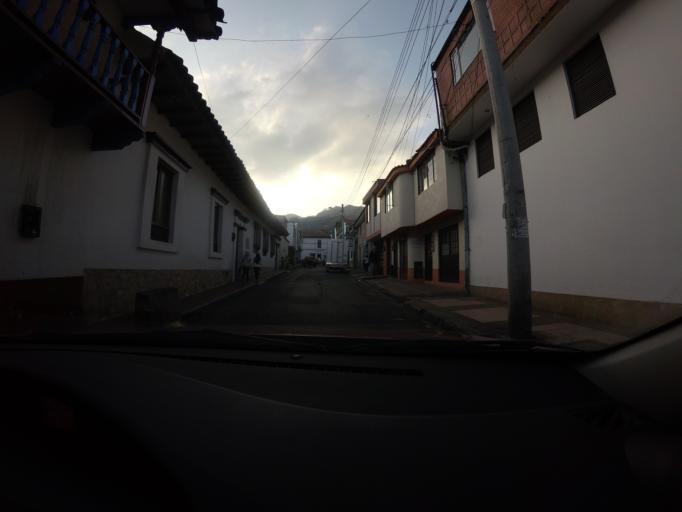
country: CO
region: Cundinamarca
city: Zipaquira
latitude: 5.0229
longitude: -74.0050
